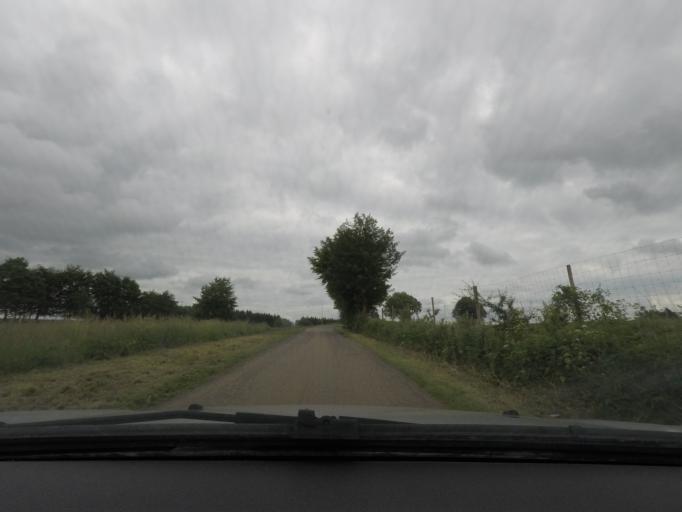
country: BE
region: Wallonia
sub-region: Province du Luxembourg
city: Leglise
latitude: 49.8336
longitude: 5.5094
